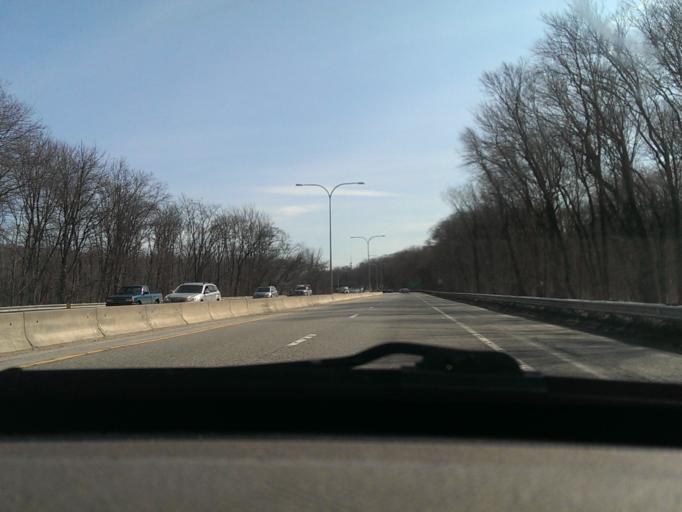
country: US
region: Rhode Island
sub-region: Providence County
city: North Providence
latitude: 41.8993
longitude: -71.4460
